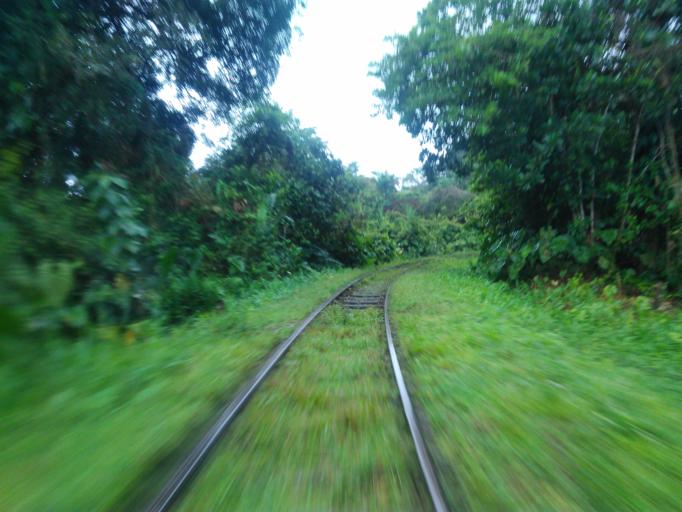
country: CO
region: Valle del Cauca
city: Buenaventura
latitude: 3.8440
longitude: -76.8785
